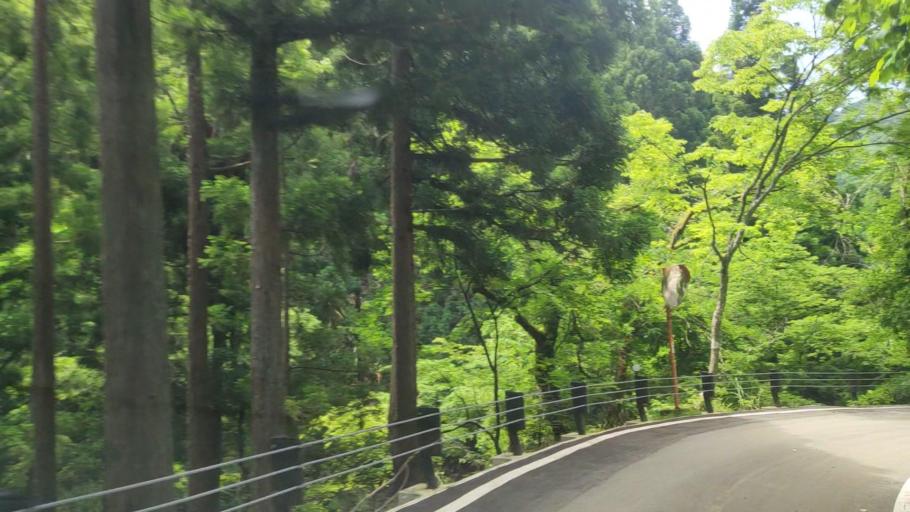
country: JP
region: Tottori
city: Tottori
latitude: 35.4143
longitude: 134.5109
